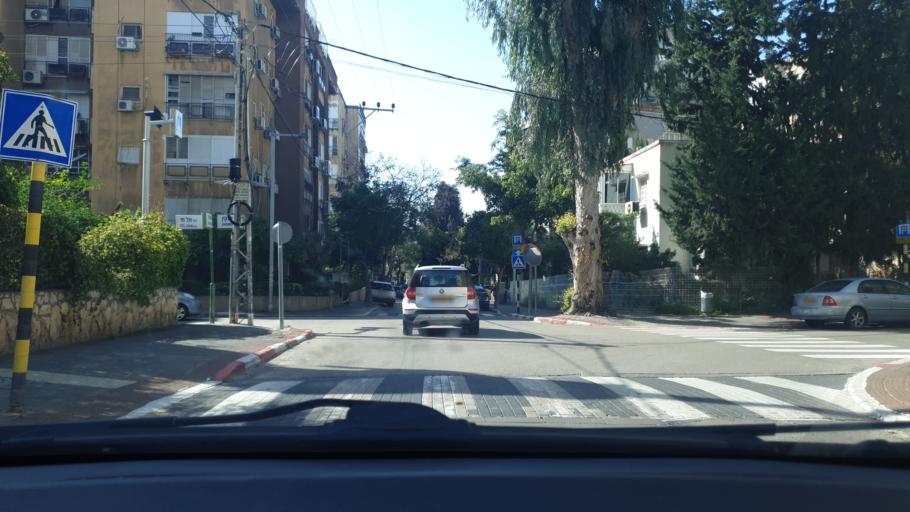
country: IL
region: Central District
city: Rishon LeZiyyon
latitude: 31.9701
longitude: 34.8006
